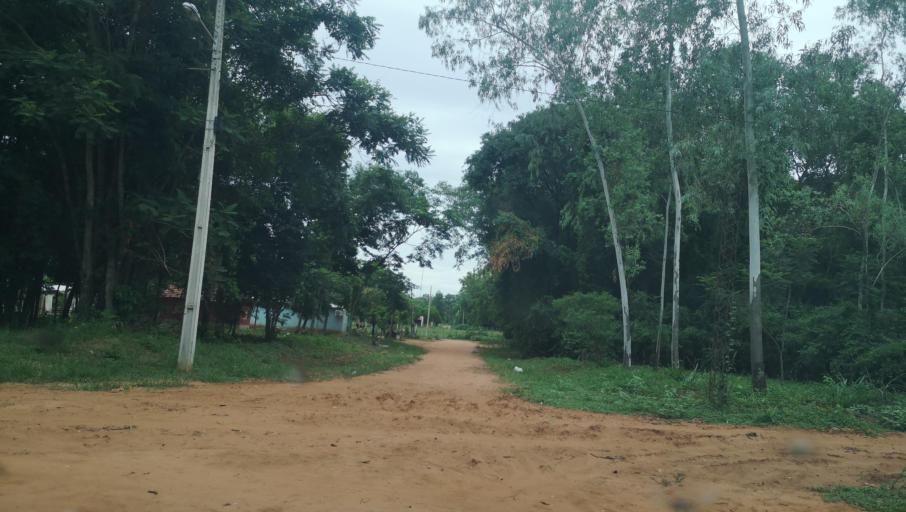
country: PY
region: San Pedro
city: Capiibary
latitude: -24.7374
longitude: -56.0193
